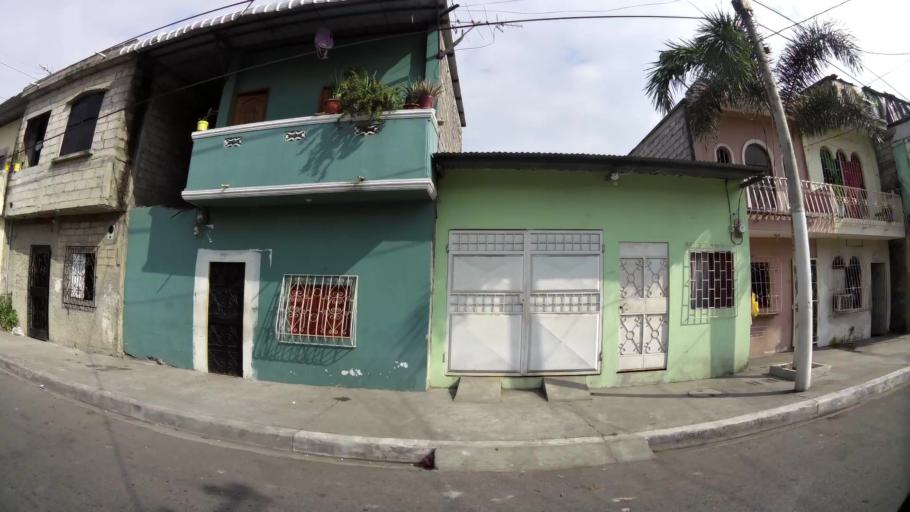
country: EC
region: Guayas
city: Guayaquil
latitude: -2.2493
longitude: -79.9091
